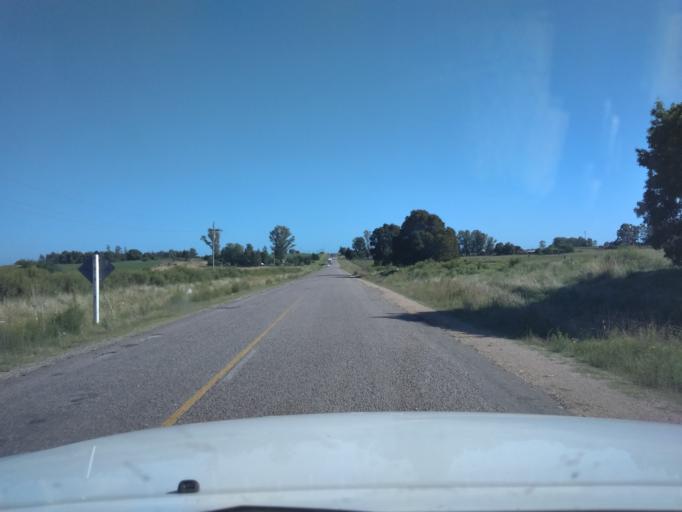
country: UY
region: Canelones
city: San Ramon
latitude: -34.2586
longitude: -55.9269
